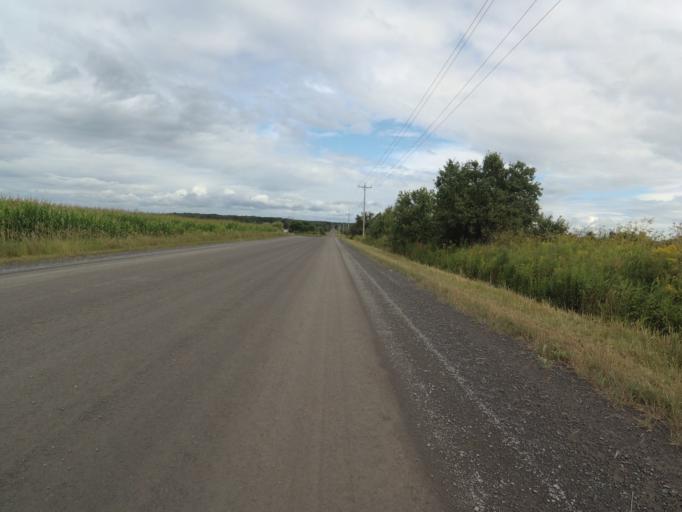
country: CA
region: Ontario
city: Clarence-Rockland
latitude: 45.4580
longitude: -75.2966
